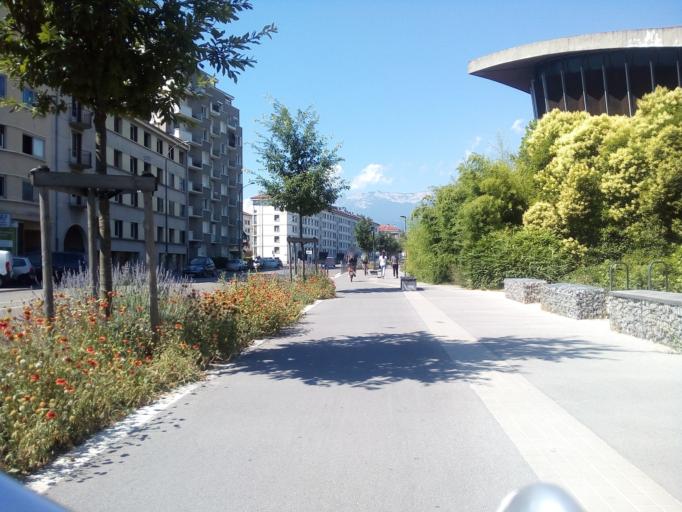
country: FR
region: Rhone-Alpes
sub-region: Departement de l'Isere
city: La Tronche
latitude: 45.1853
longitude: 5.7419
